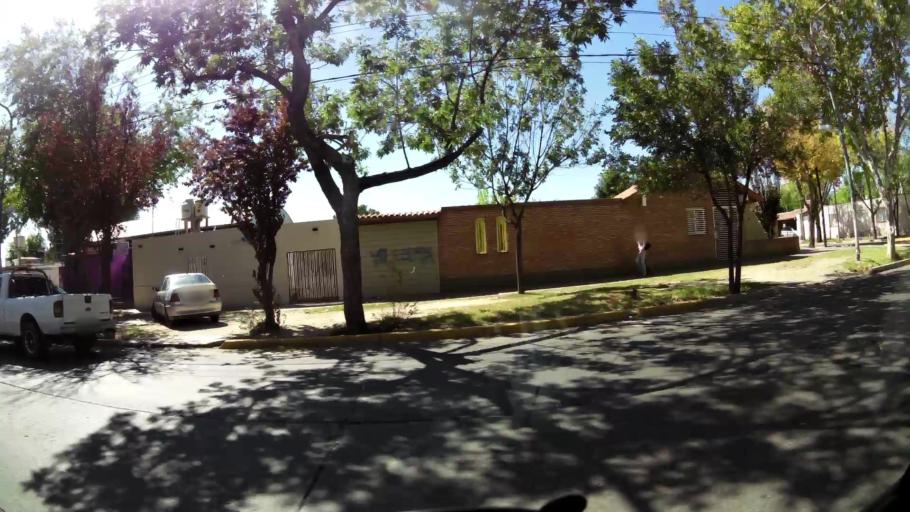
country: AR
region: Mendoza
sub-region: Departamento de Godoy Cruz
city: Godoy Cruz
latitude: -32.9184
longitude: -68.8595
